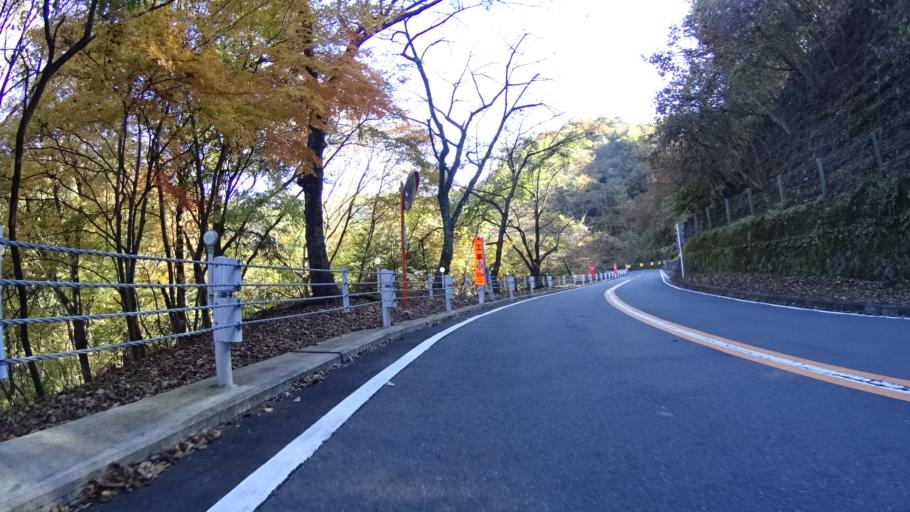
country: JP
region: Yamanashi
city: Uenohara
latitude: 35.7564
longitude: 139.0292
